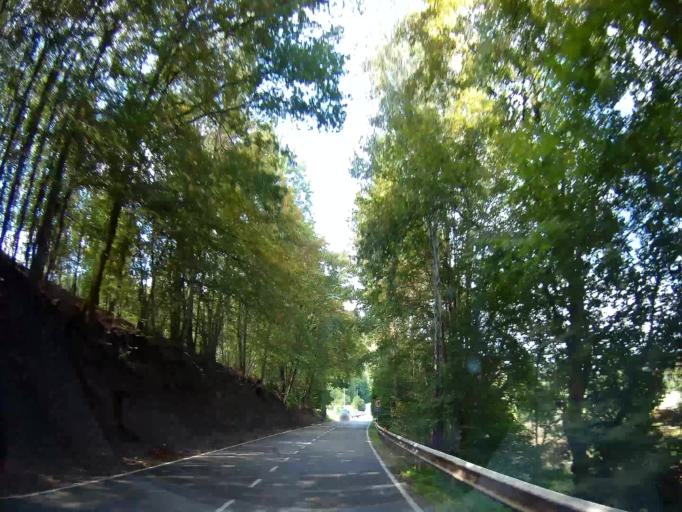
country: BE
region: Wallonia
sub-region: Province du Luxembourg
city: La Roche-en-Ardenne
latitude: 50.1951
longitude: 5.5380
